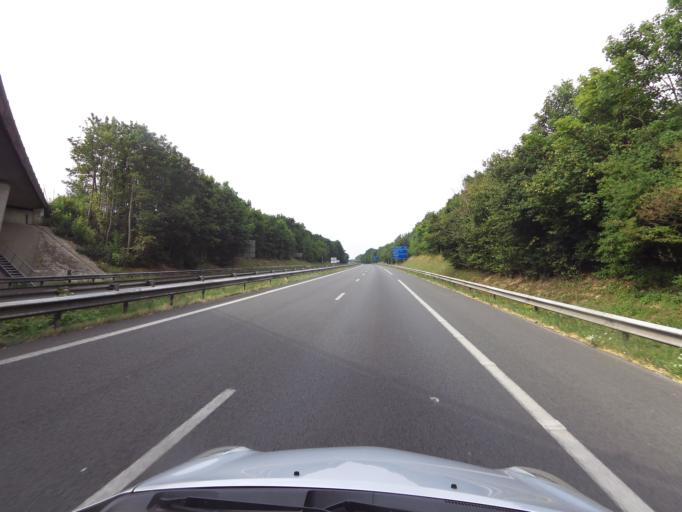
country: FR
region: Nord-Pas-de-Calais
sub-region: Departement du Pas-de-Calais
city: Marquion
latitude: 50.2072
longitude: 3.1013
